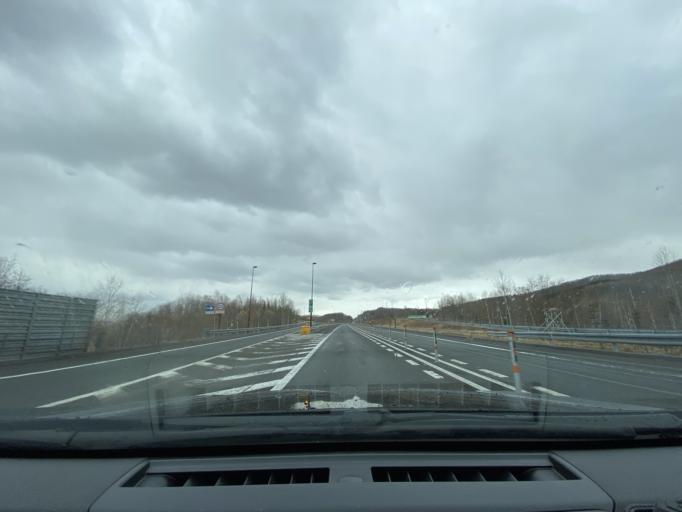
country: JP
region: Hokkaido
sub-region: Asahikawa-shi
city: Asahikawa
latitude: 43.8931
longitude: 142.4598
